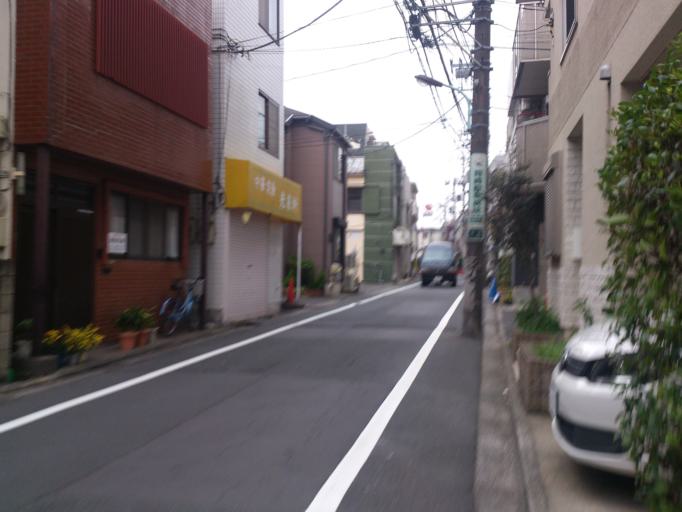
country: JP
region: Tokyo
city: Tokyo
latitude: 35.6624
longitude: 139.6740
